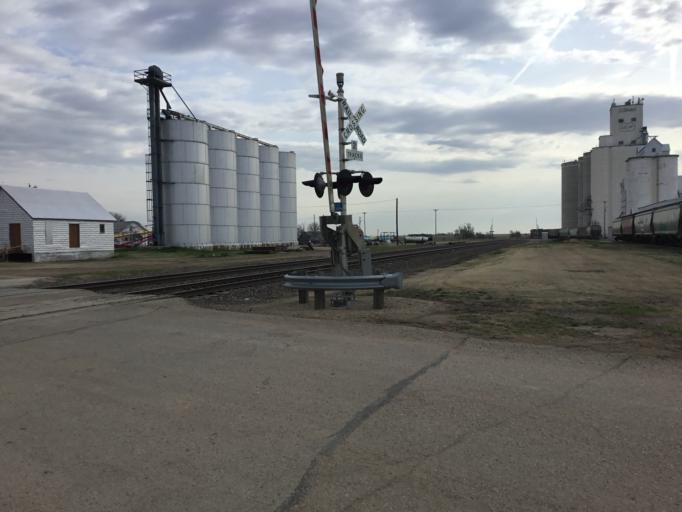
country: US
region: Kansas
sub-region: Ellis County
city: Victoria
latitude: 38.8808
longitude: -99.0236
